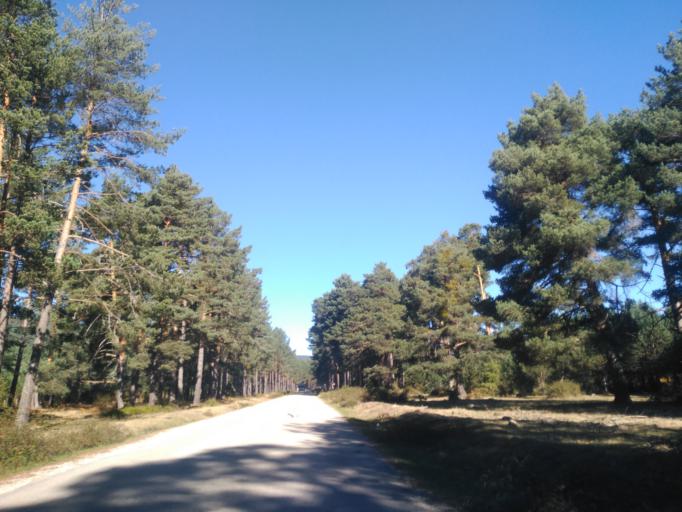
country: ES
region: Castille and Leon
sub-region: Provincia de Soria
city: Vinuesa
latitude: 41.9795
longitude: -2.7950
